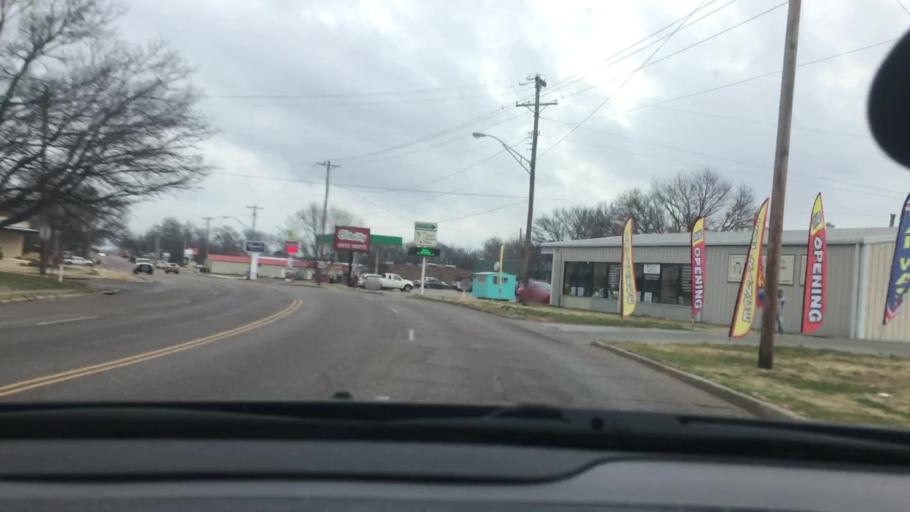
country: US
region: Oklahoma
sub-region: Johnston County
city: Tishomingo
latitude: 34.2307
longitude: -96.6704
